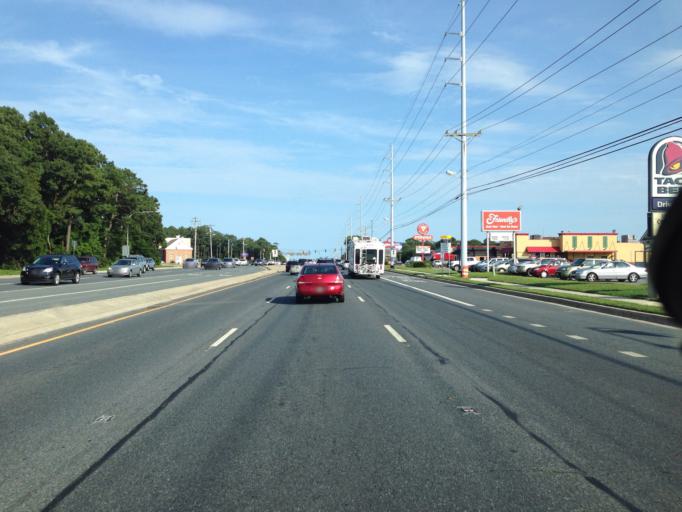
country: US
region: Delaware
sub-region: Sussex County
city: Lewes
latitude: 38.7296
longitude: -75.1313
